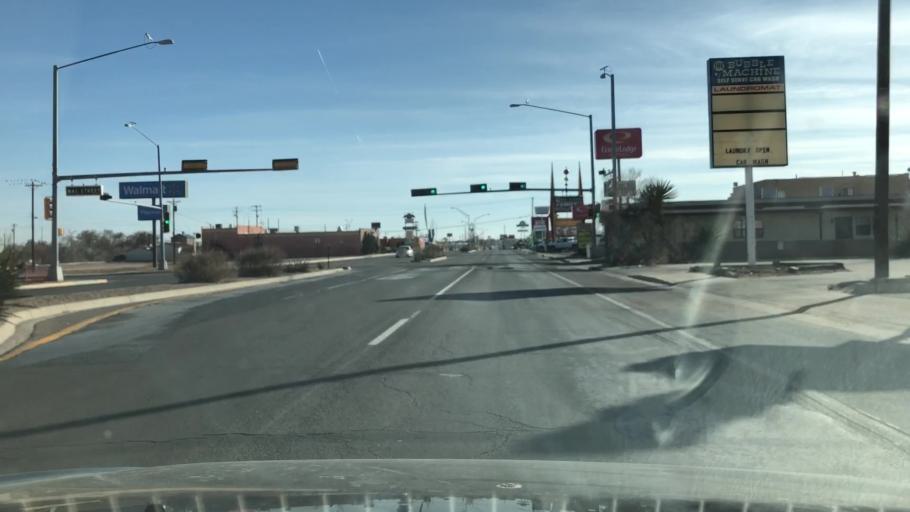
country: US
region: New Mexico
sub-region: Socorro County
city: Socorro
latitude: 34.0654
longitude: -106.8927
